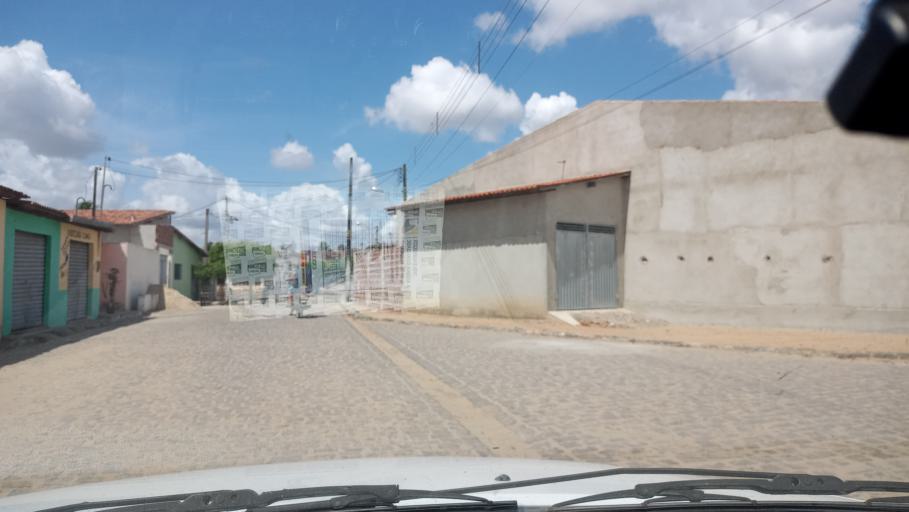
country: BR
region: Rio Grande do Norte
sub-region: Santo Antonio
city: Santo Antonio
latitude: -6.3486
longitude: -35.3731
